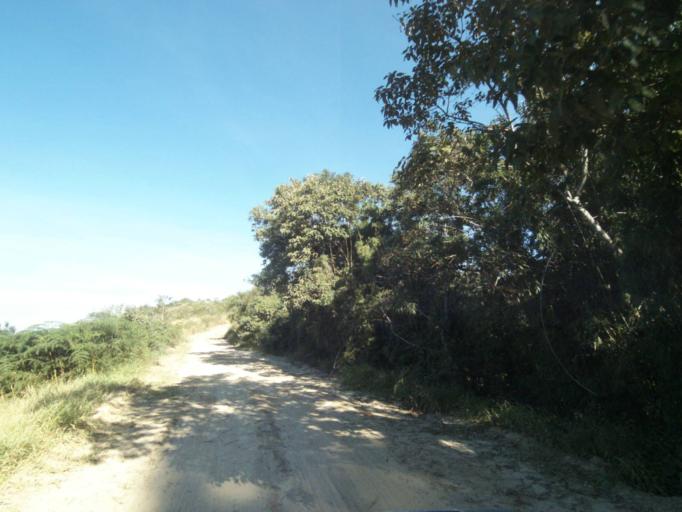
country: BR
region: Parana
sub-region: Tibagi
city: Tibagi
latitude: -24.5631
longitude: -50.4717
